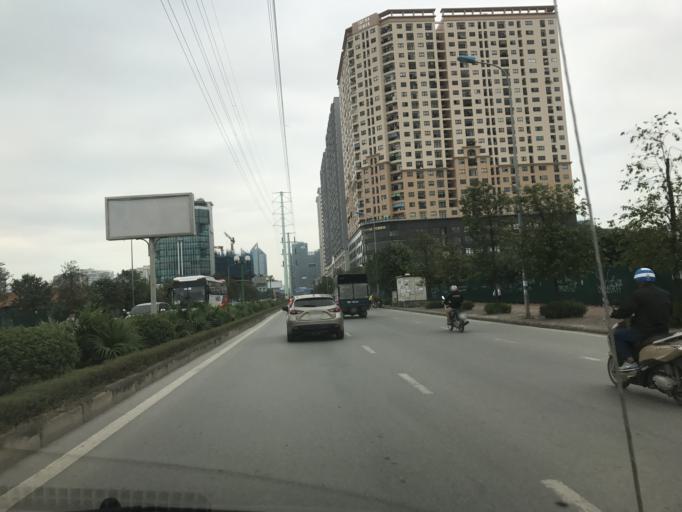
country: VN
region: Ha Noi
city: Thanh Xuan
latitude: 20.9956
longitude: 105.7914
